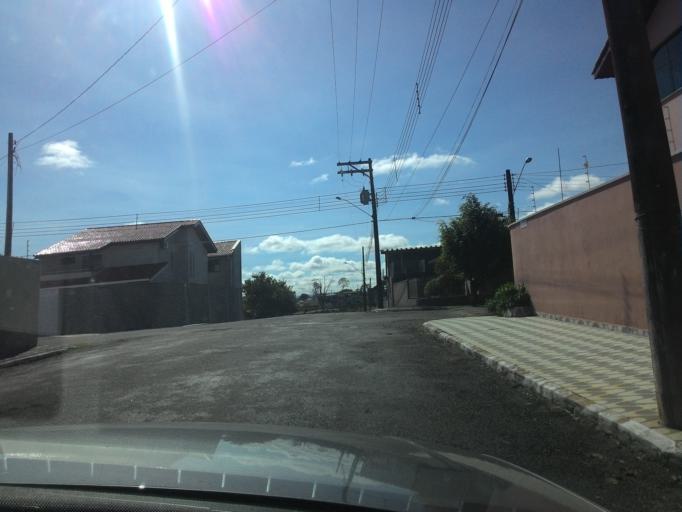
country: BR
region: Sao Paulo
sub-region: Registro
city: Registro
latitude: -24.4992
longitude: -47.8377
